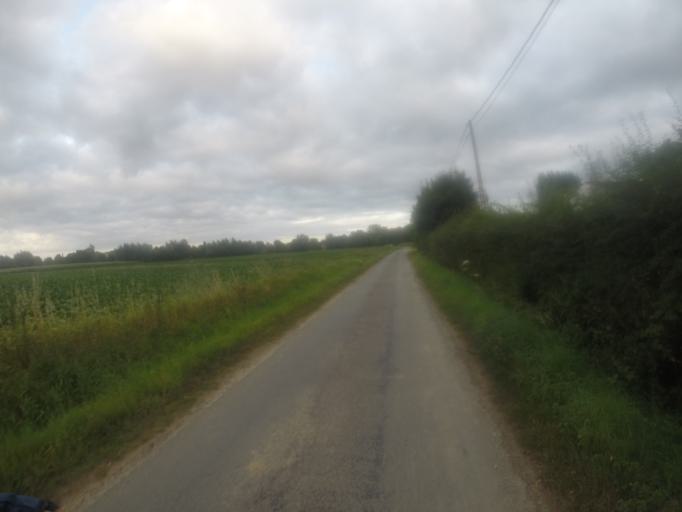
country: BE
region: Flanders
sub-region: Provincie West-Vlaanderen
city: Poperinge
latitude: 50.8469
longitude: 2.7053
